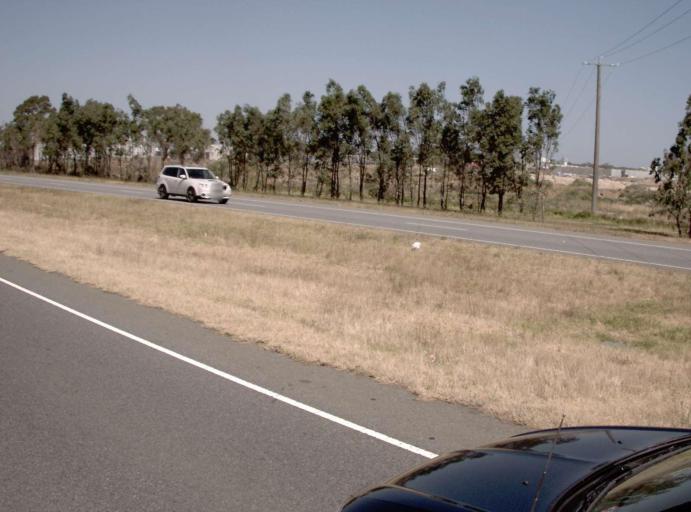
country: AU
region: Victoria
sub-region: Greater Dandenong
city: Dandenong
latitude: -38.0019
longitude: 145.1979
